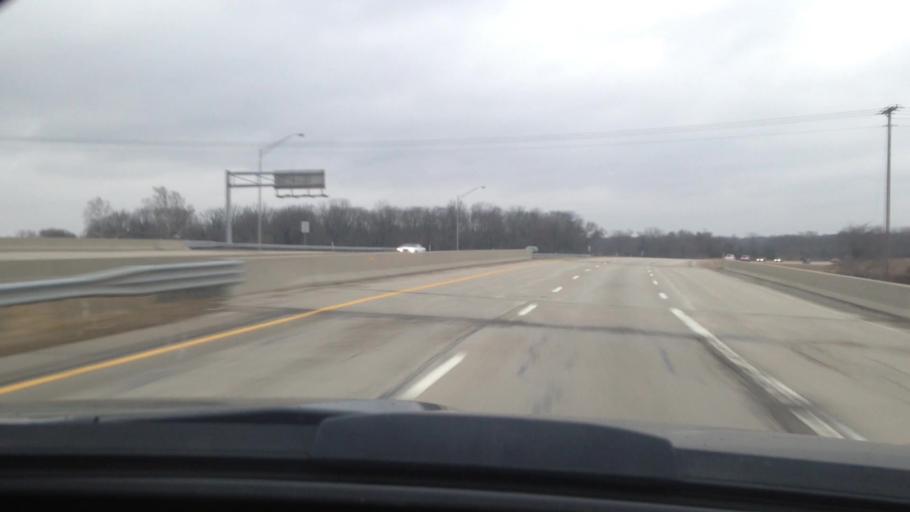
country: US
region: Indiana
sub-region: Delaware County
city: Muncie
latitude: 40.1789
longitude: -85.3366
